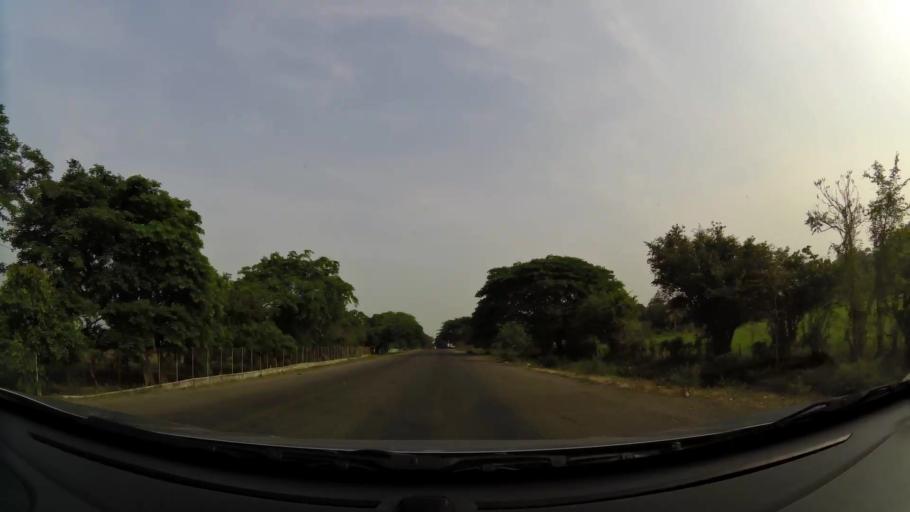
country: HN
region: Comayagua
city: Flores
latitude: 14.2780
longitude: -87.5624
